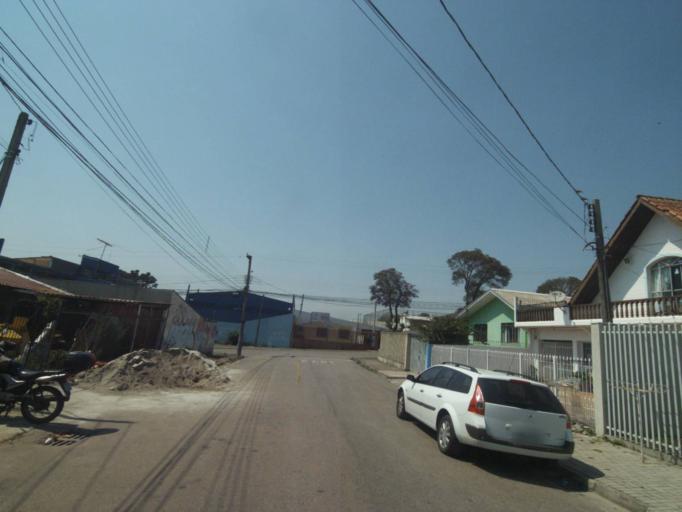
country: BR
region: Parana
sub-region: Sao Jose Dos Pinhais
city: Sao Jose dos Pinhais
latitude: -25.5151
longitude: -49.2775
